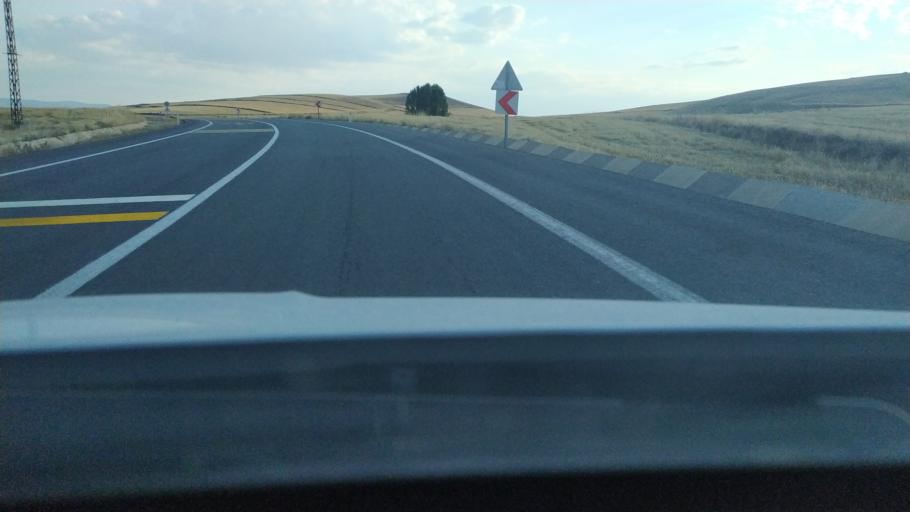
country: TR
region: Kayseri
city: Muncusun
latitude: 38.9531
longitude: 35.7515
